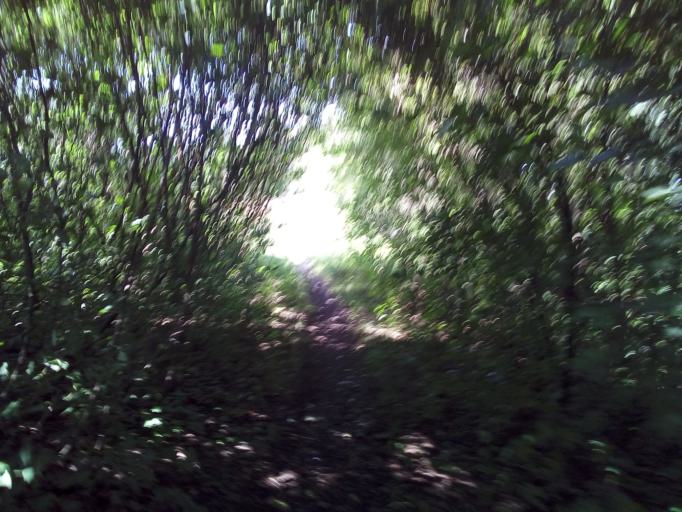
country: DE
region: Bavaria
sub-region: Upper Bavaria
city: Unterfoehring
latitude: 48.1725
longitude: 11.6608
